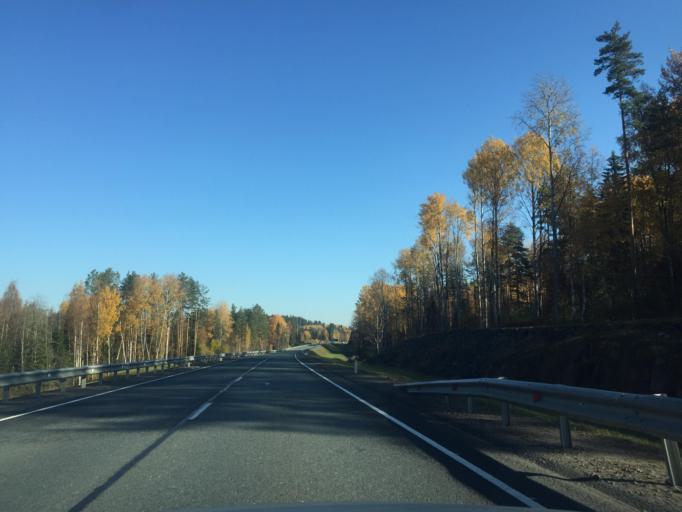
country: RU
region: Leningrad
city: Kuznechnoye
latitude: 61.3284
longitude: 29.8168
